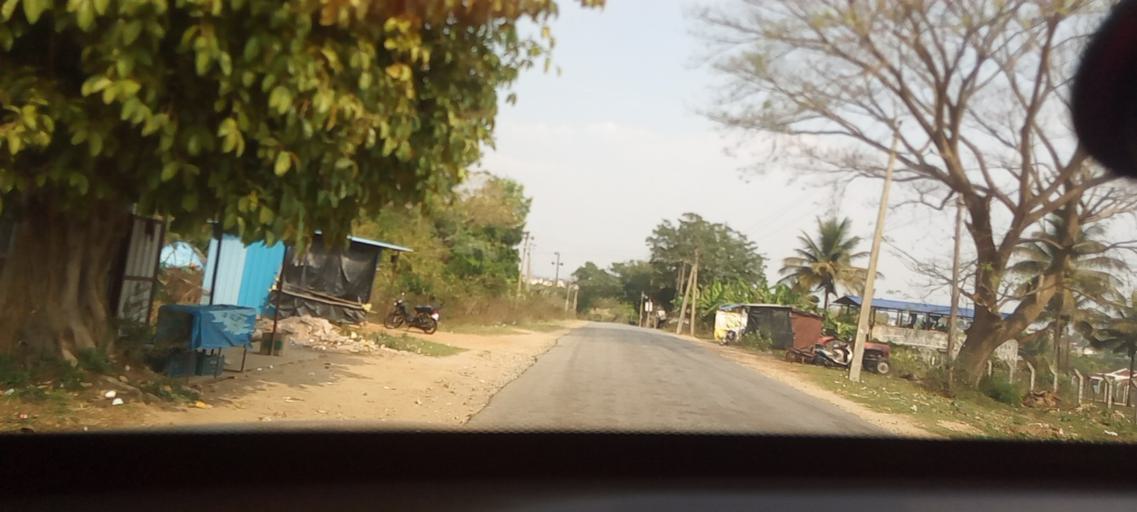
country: IN
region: Karnataka
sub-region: Hassan
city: Belur
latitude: 13.1736
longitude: 75.8573
